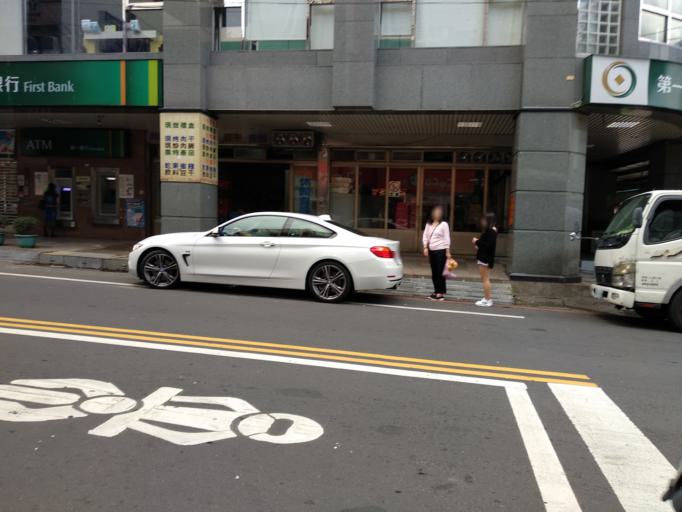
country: TW
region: Taiwan
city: Daxi
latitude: 24.7914
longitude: 121.1763
